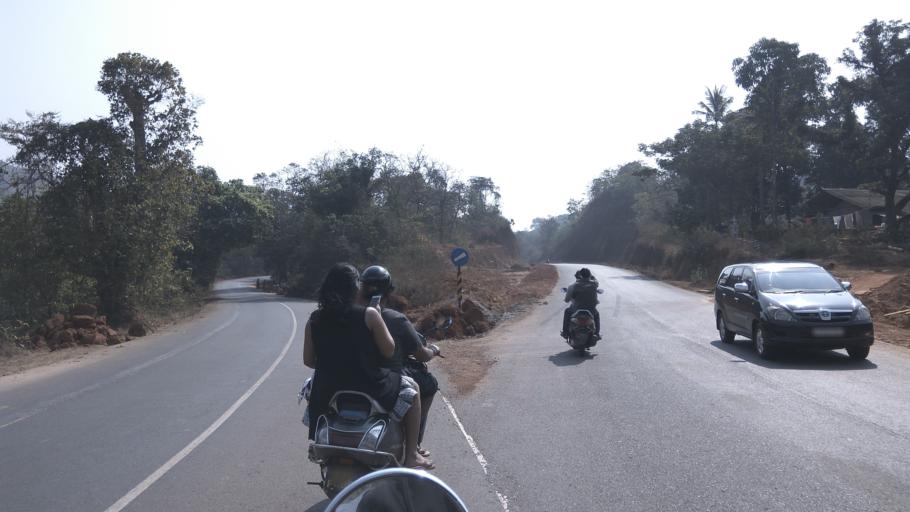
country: IN
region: Goa
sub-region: North Goa
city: Palle
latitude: 15.3870
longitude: 74.1318
